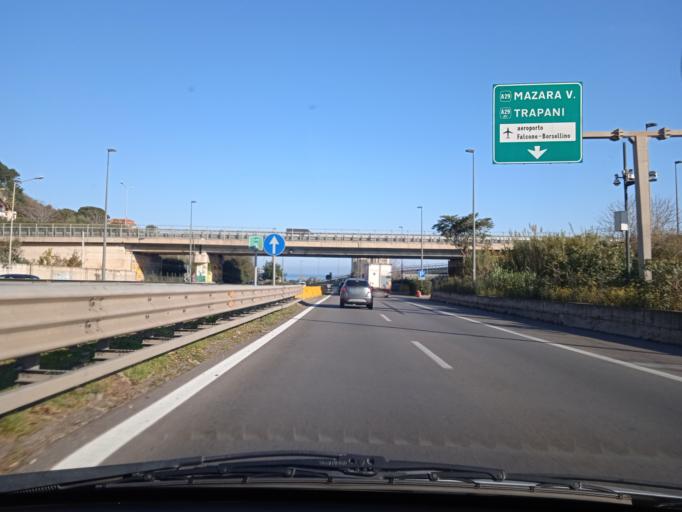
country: IT
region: Sicily
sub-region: Palermo
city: Isola delle Femmine
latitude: 38.1897
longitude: 13.2829
